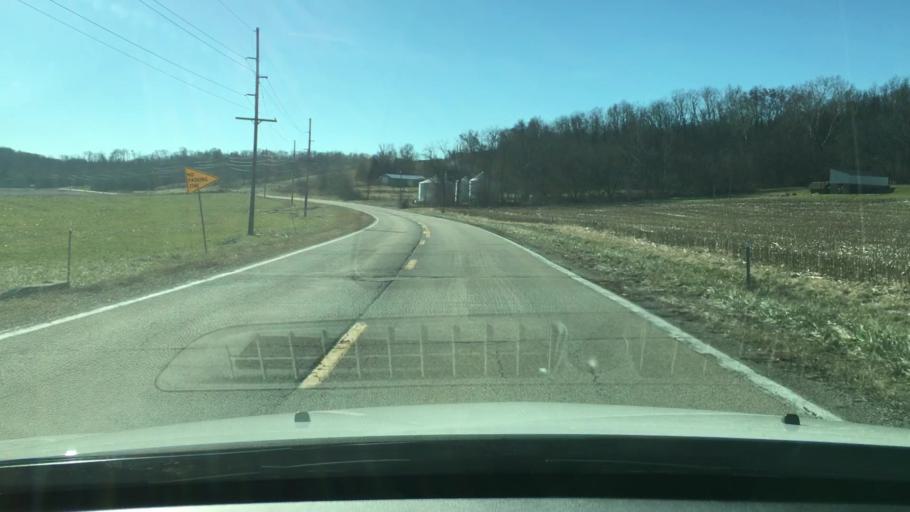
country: US
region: Illinois
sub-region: Fulton County
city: Astoria
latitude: 40.2233
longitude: -90.2070
